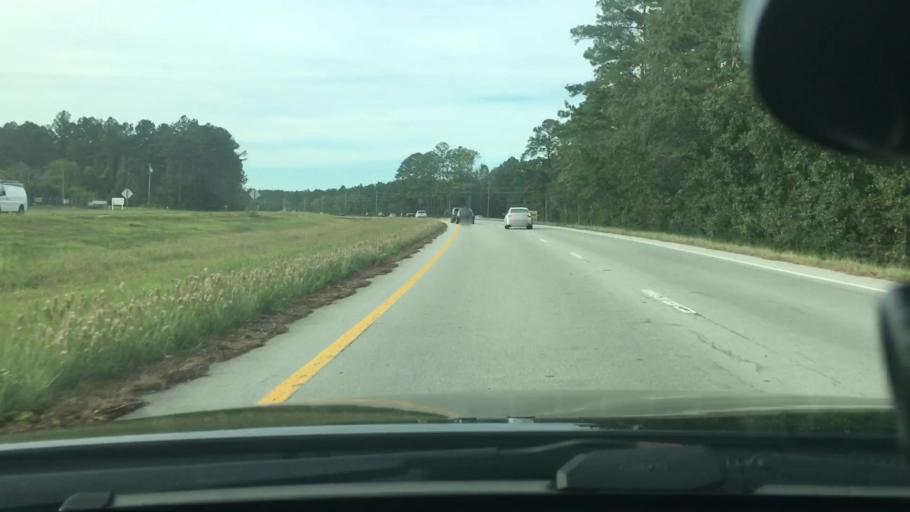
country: US
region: North Carolina
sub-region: Craven County
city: Neuse Forest
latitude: 34.9572
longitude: -76.9505
